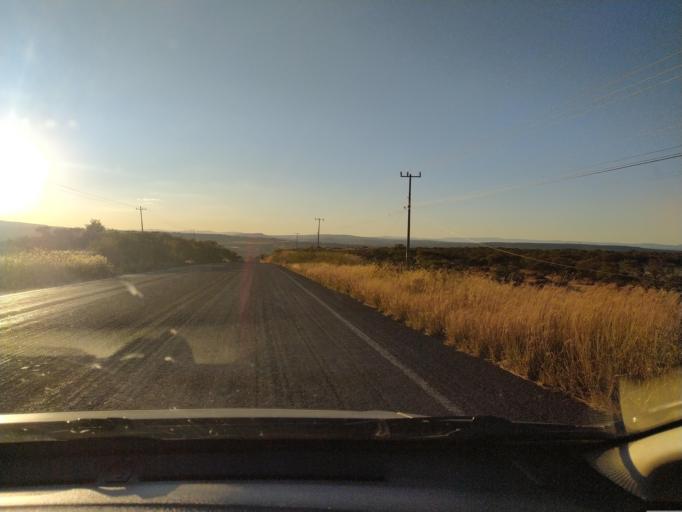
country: MX
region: Jalisco
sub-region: San Julian
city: Colonia Veintitres de Mayo
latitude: 21.0087
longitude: -102.2598
